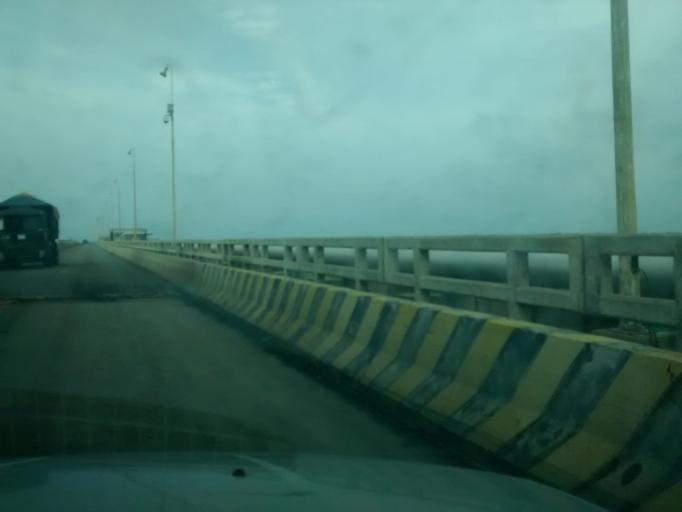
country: BR
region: Ceara
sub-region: Caucaia
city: Cambebba
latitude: -3.5353
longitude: -38.7983
